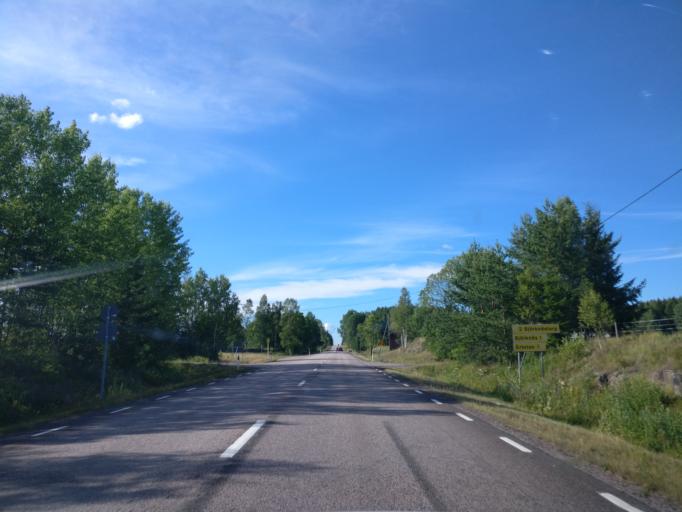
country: SE
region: Vaermland
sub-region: Karlstads Kommun
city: Edsvalla
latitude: 59.5800
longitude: 13.0172
